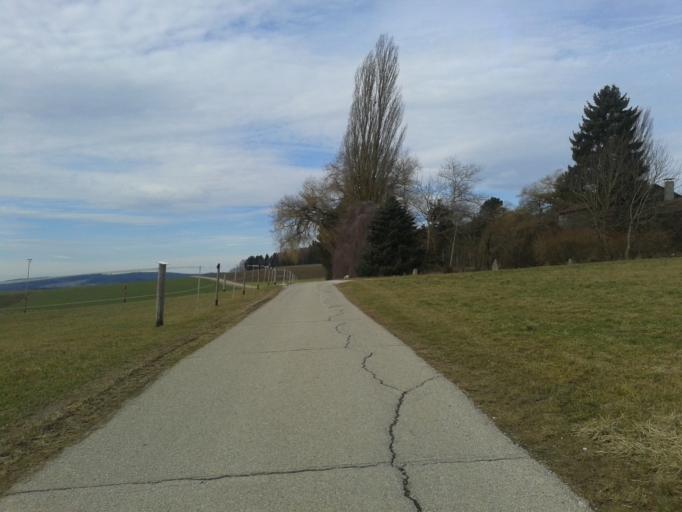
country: DE
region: Baden-Wuerttemberg
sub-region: Tuebingen Region
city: Altheim
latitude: 48.3110
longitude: 9.7606
